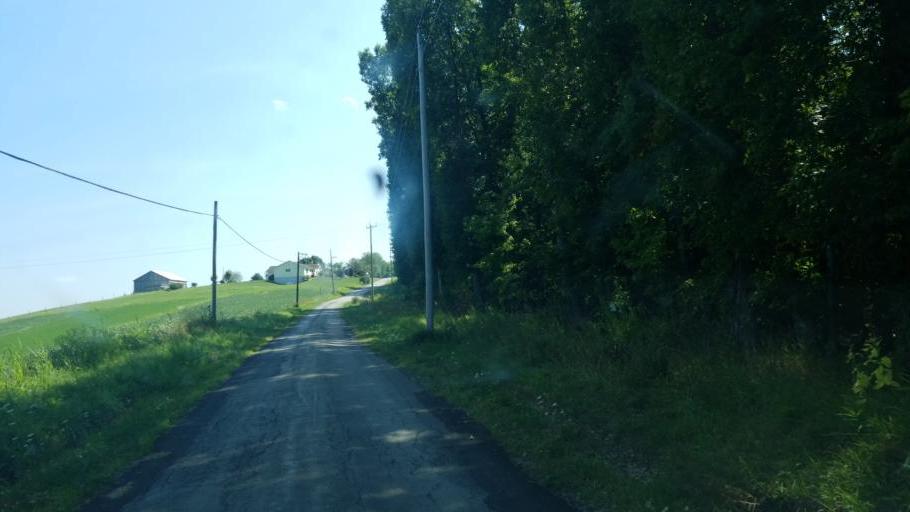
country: US
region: Pennsylvania
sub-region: Clarion County
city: Knox
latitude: 41.0983
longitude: -79.5232
